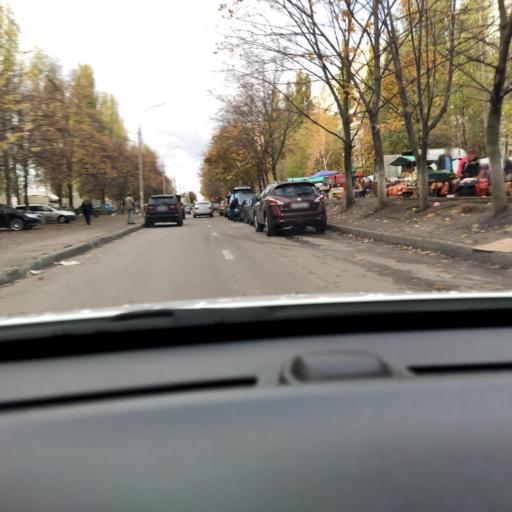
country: RU
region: Voronezj
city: Podgornoye
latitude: 51.7039
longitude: 39.1634
